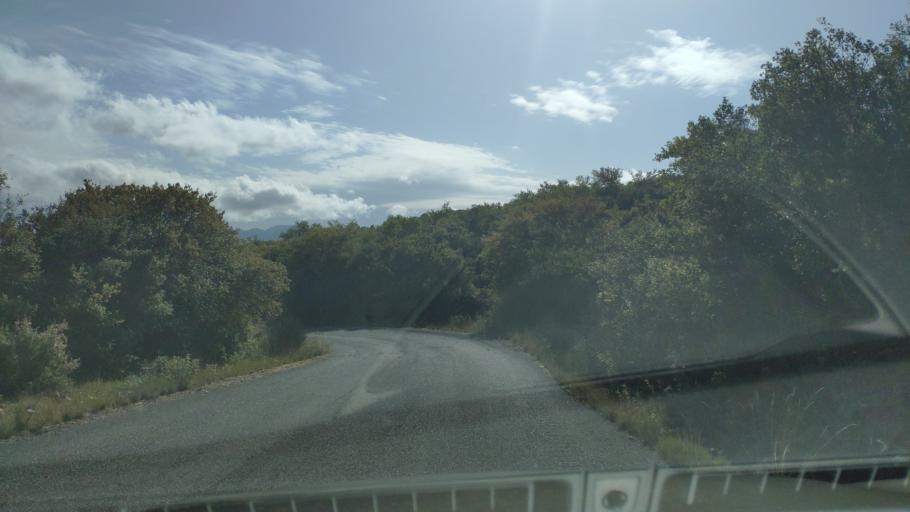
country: GR
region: Peloponnese
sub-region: Nomos Arkadias
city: Dimitsana
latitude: 37.5691
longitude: 22.0069
